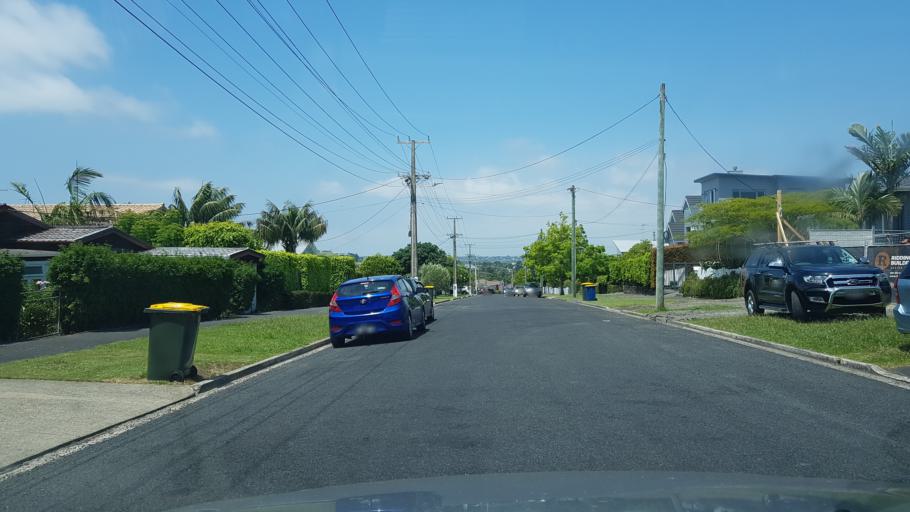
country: NZ
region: Auckland
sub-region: Auckland
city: North Shore
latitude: -36.8095
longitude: 174.7968
